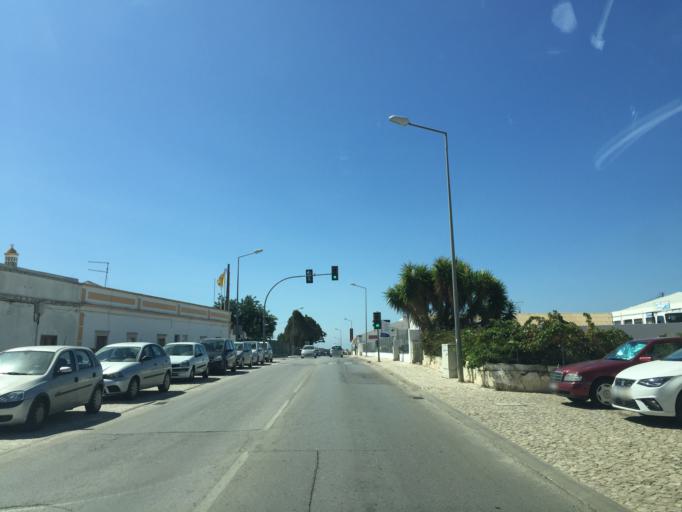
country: PT
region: Faro
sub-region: Albufeira
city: Ferreiras
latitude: 37.1247
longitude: -8.2446
